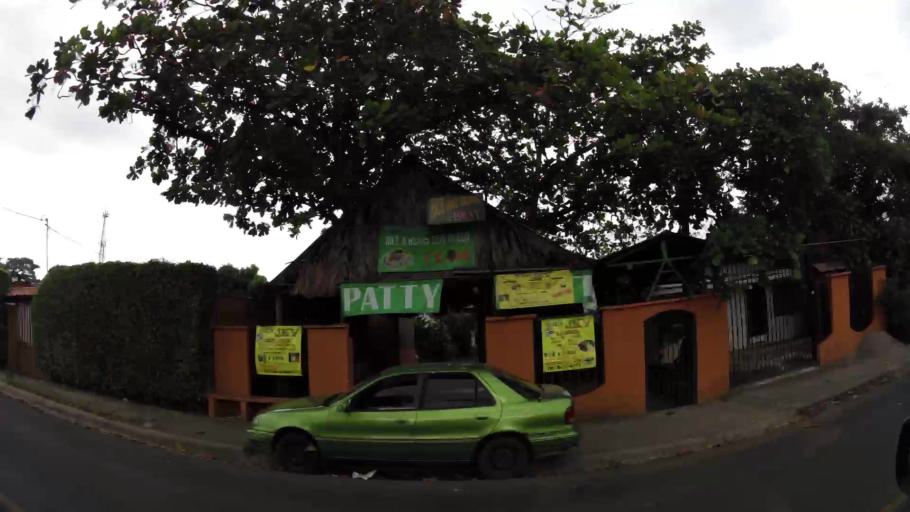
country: CR
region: San Jose
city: Santa Ana
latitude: 9.9517
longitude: -84.1896
